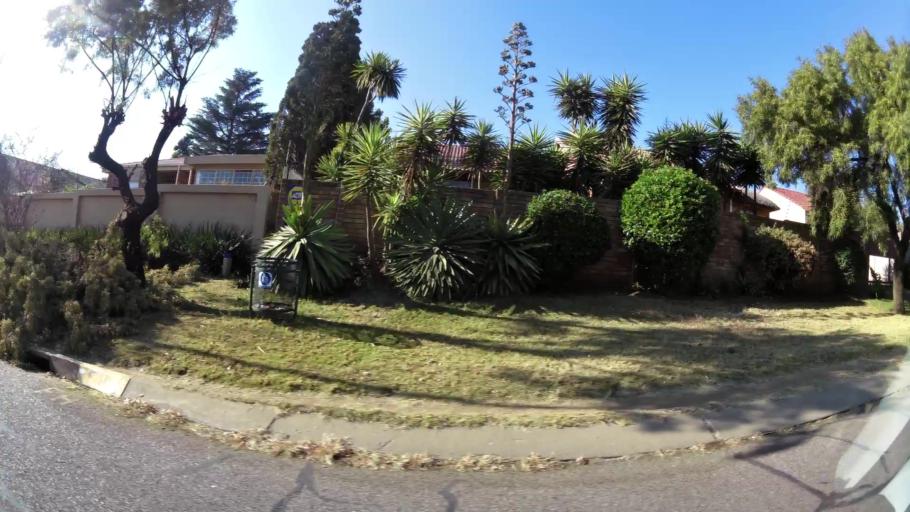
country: ZA
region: Gauteng
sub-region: City of Johannesburg Metropolitan Municipality
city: Modderfontein
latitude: -26.1373
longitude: 28.1386
